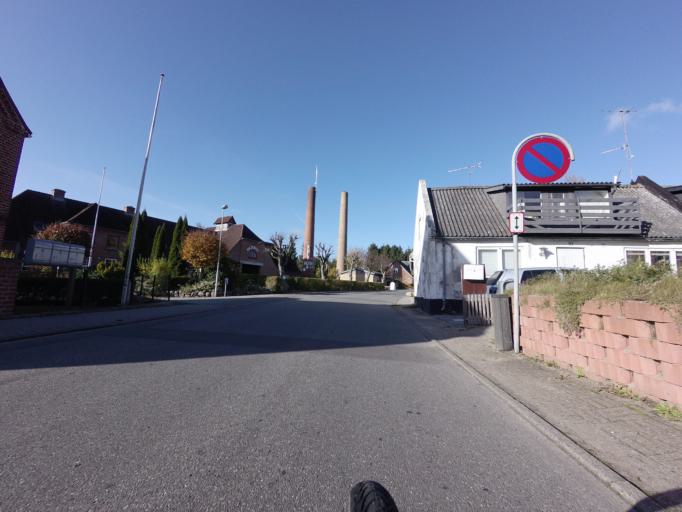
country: DK
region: Central Jutland
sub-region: Syddjurs Kommune
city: Ryomgard
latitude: 56.4093
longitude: 10.5655
